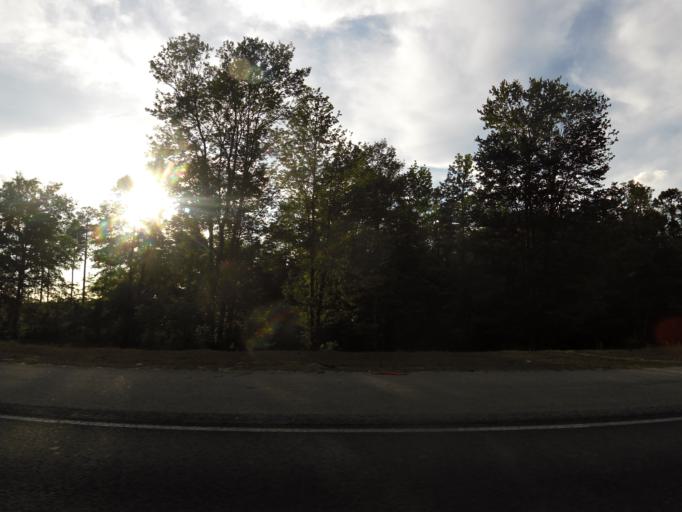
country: US
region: Georgia
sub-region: Chatham County
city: Pooler
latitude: 32.1524
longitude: -81.2381
